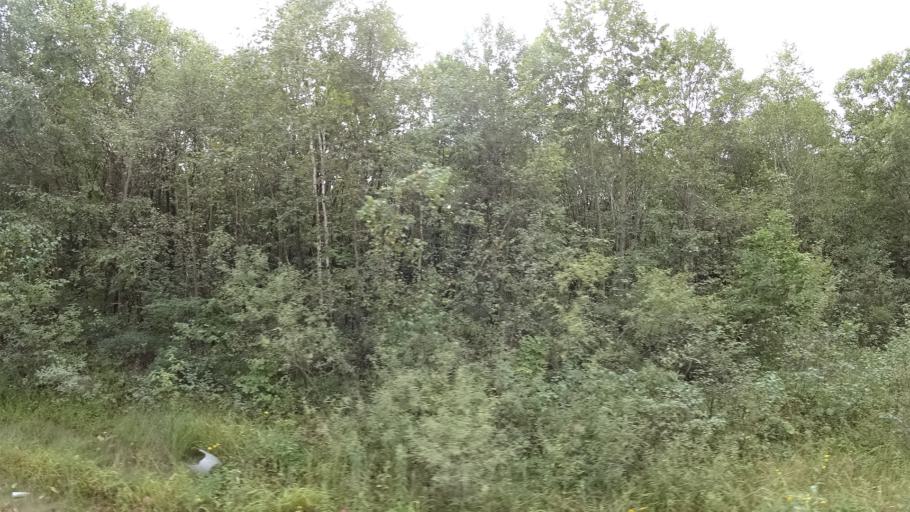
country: RU
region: Primorskiy
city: Lyalichi
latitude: 44.0864
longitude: 132.4393
